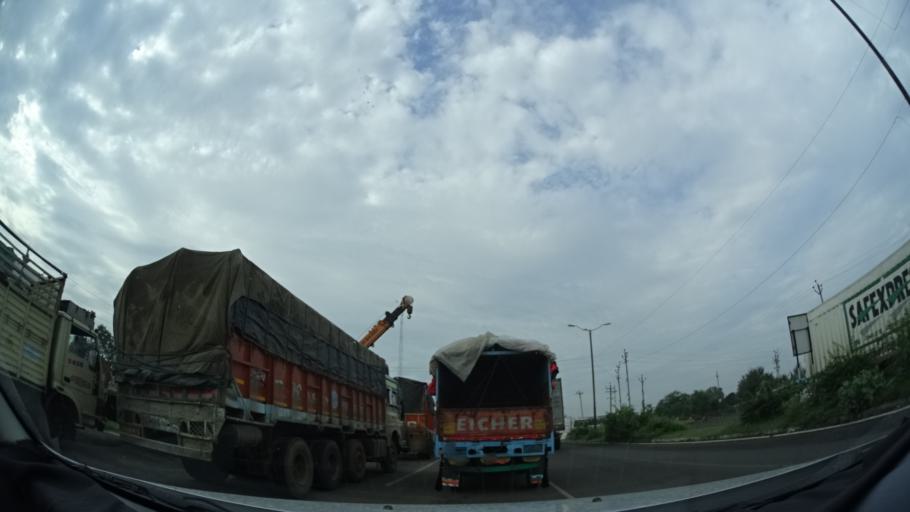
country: IN
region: Madhya Pradesh
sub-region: Bhopal
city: Bhopal
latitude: 23.2525
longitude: 77.5108
